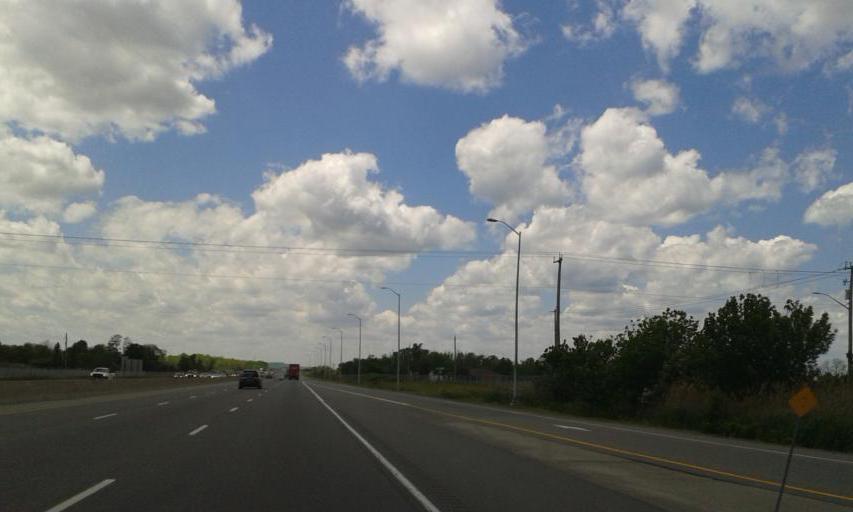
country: CA
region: Ontario
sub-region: Regional Municipality of Niagara
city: St. Catharines
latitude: 43.1875
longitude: -79.4236
